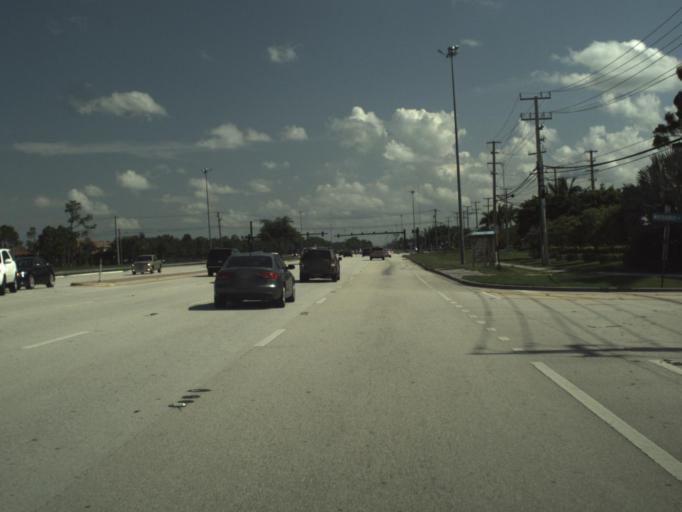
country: US
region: Florida
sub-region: Palm Beach County
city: Wellington
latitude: 26.6310
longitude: -80.2045
